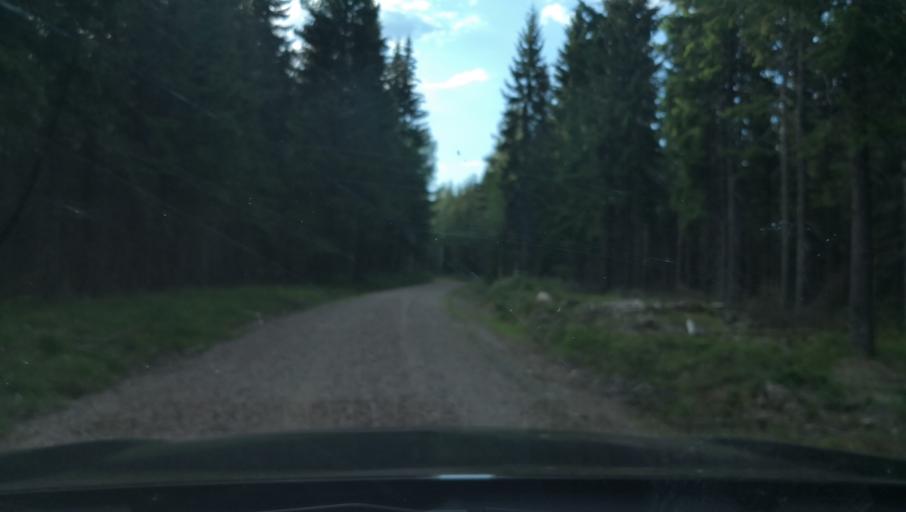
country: SE
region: Dalarna
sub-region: Ludvika Kommun
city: Ludvika
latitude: 60.0739
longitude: 15.2909
